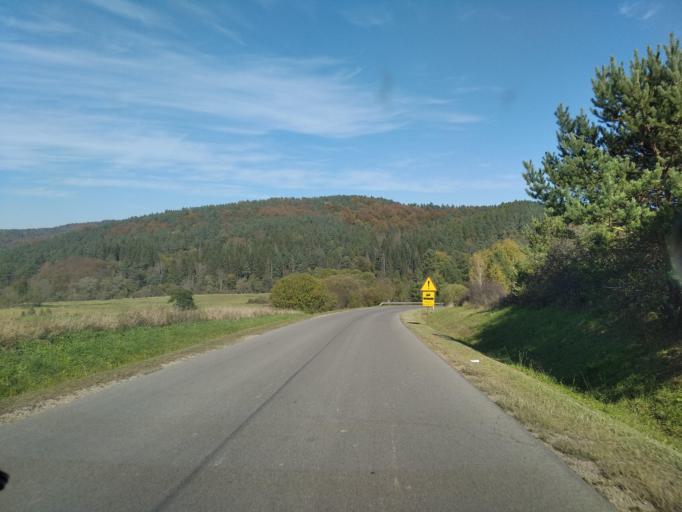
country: PL
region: Subcarpathian Voivodeship
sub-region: Powiat sanocki
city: Bukowsko
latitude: 49.4176
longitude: 21.9556
